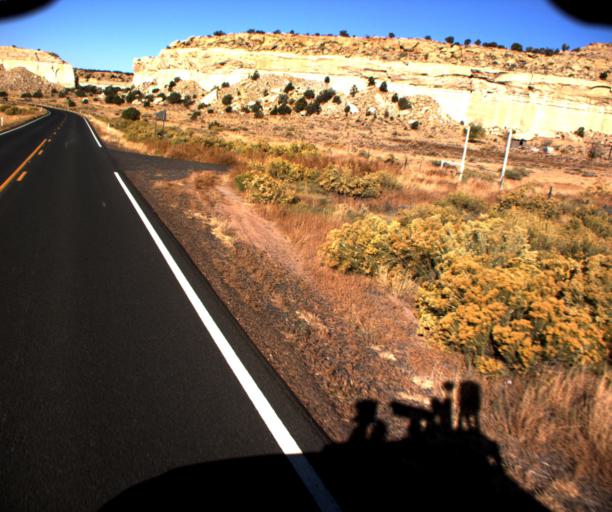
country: US
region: Arizona
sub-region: Apache County
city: Ganado
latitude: 35.7561
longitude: -109.8307
